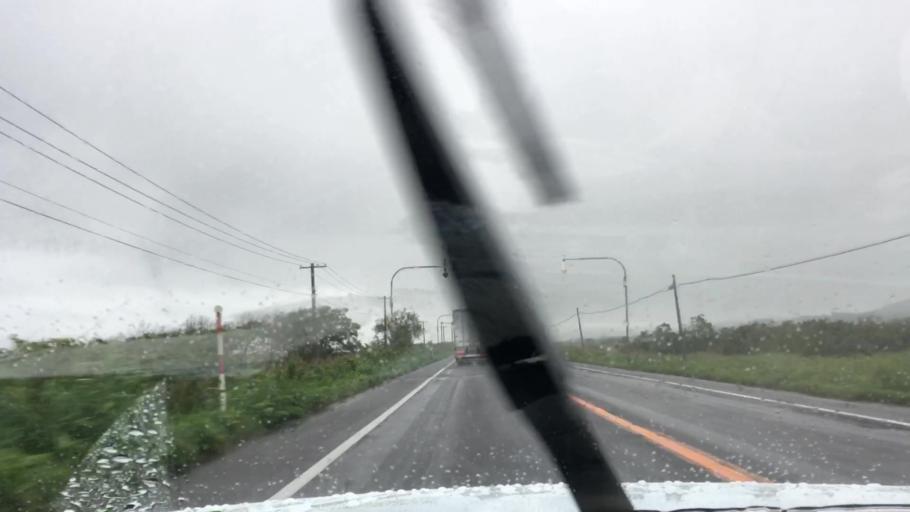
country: JP
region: Hokkaido
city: Niseko Town
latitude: 42.4293
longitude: 140.3176
